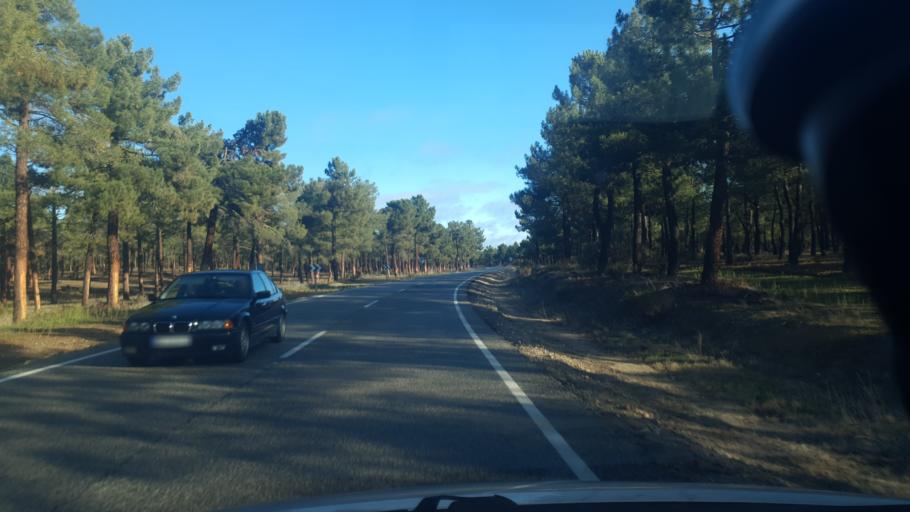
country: ES
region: Castille and Leon
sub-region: Provincia de Avila
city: Tinosillos
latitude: 40.9549
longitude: -4.7099
